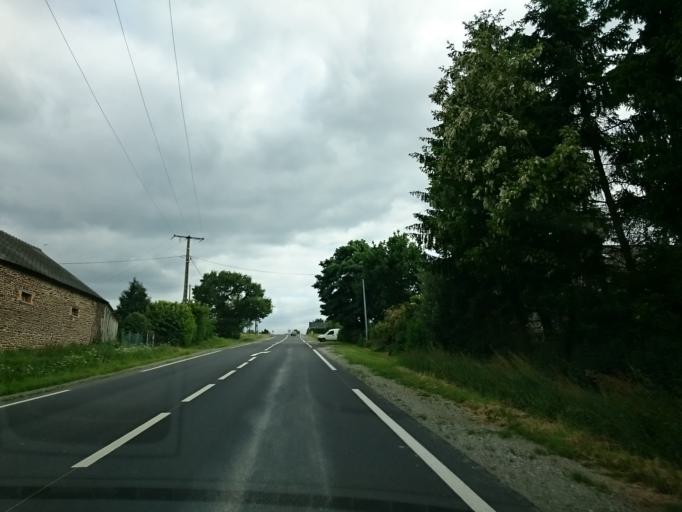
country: FR
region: Brittany
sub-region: Departement d'Ille-et-Vilaine
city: Crevin
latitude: 47.9319
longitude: -1.6748
